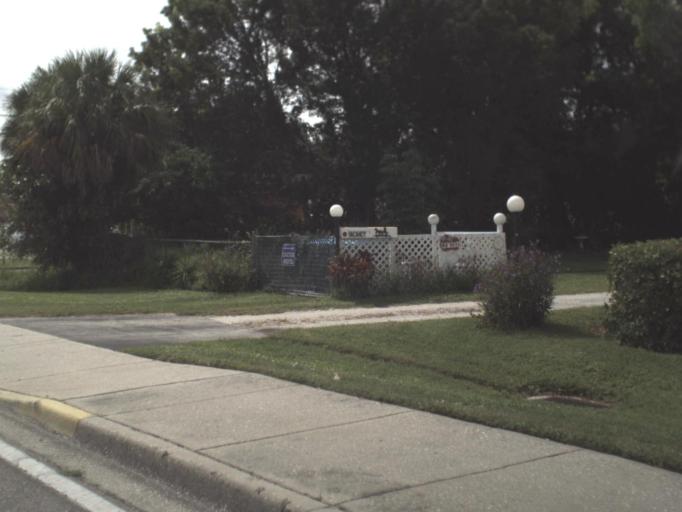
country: US
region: Florida
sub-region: Lee County
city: North Fort Myers
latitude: 26.6788
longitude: -81.8833
